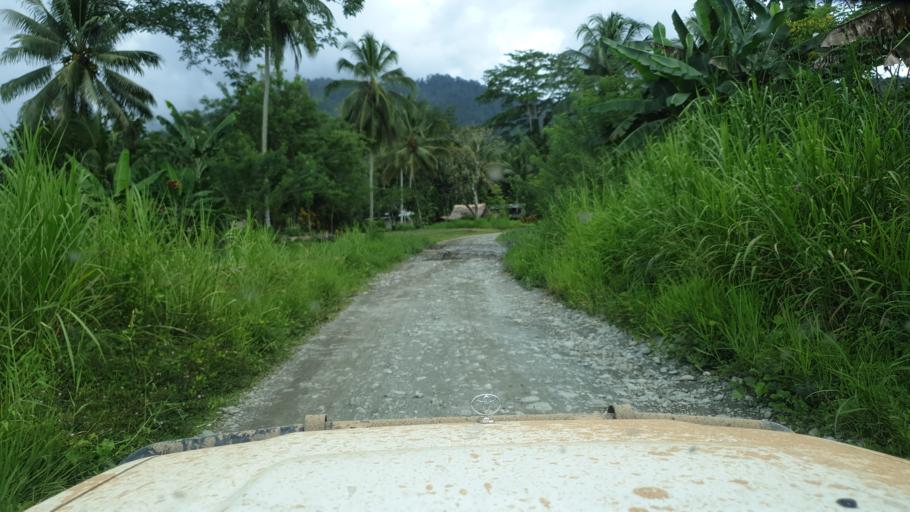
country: PG
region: Northern Province
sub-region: Sohe
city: Kokoda
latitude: -8.9170
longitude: 147.8722
